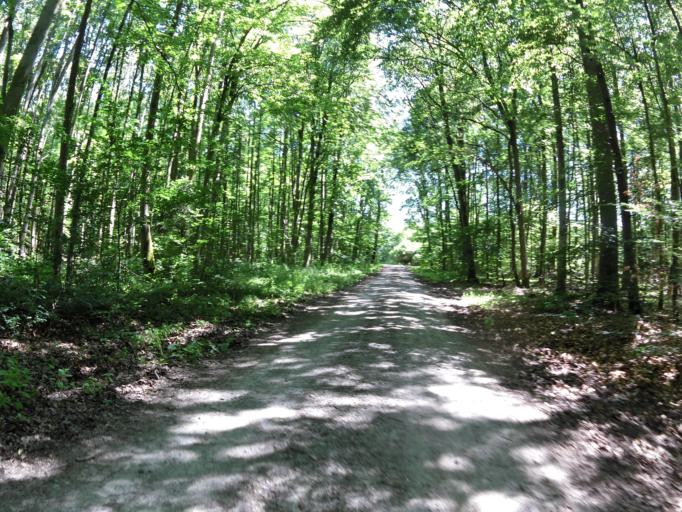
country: DE
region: Bavaria
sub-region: Regierungsbezirk Unterfranken
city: Kleinrinderfeld
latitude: 49.7148
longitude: 9.8725
